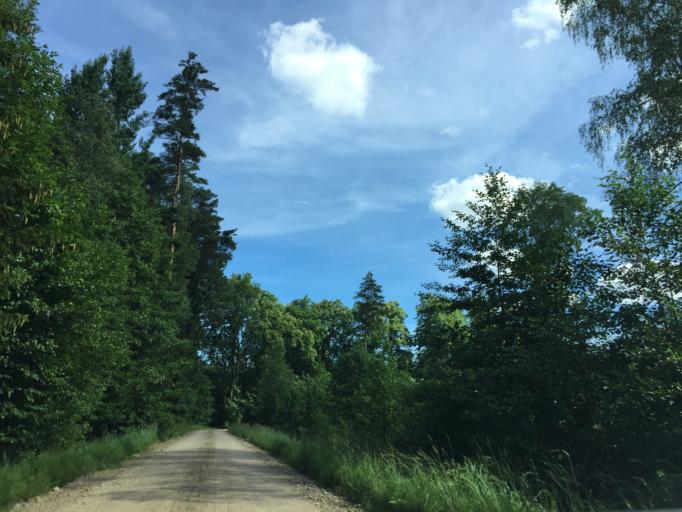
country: LV
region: Dundaga
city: Dundaga
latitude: 57.4264
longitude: 22.0744
